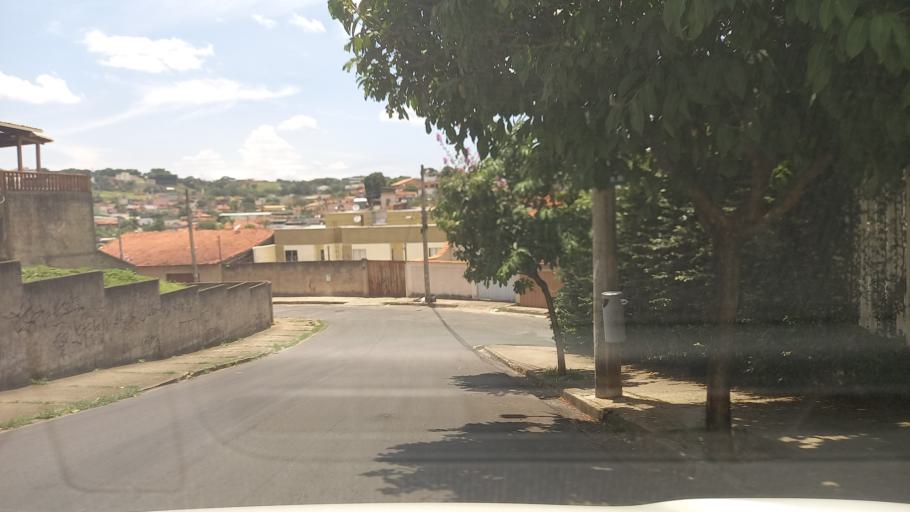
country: BR
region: Minas Gerais
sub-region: Contagem
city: Contagem
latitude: -19.9140
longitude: -44.0047
